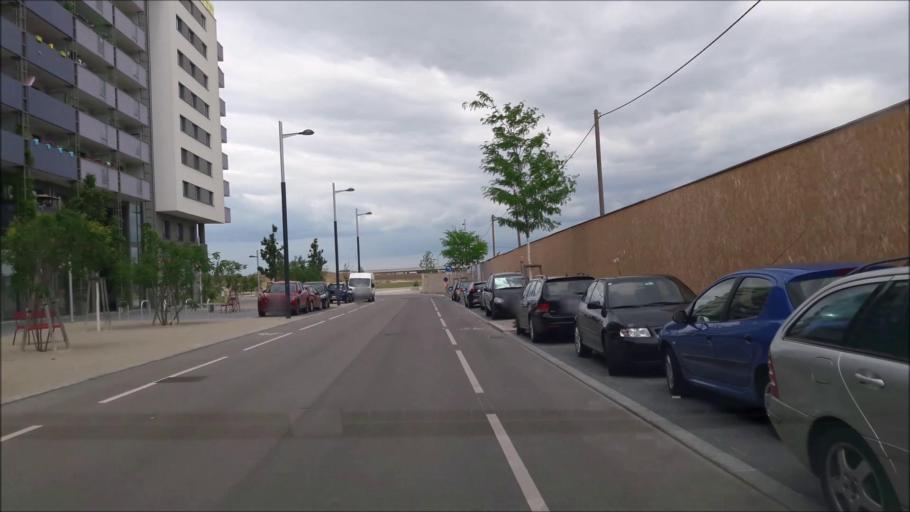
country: AT
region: Lower Austria
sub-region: Politischer Bezirk Ganserndorf
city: Gross-Enzersdorf
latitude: 48.2259
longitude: 16.5038
